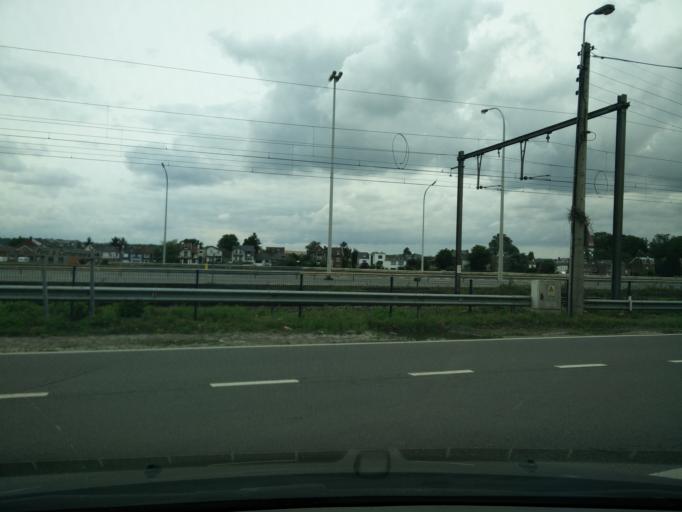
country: BE
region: Wallonia
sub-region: Province de Liege
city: Vise
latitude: 50.7122
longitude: 5.6861
